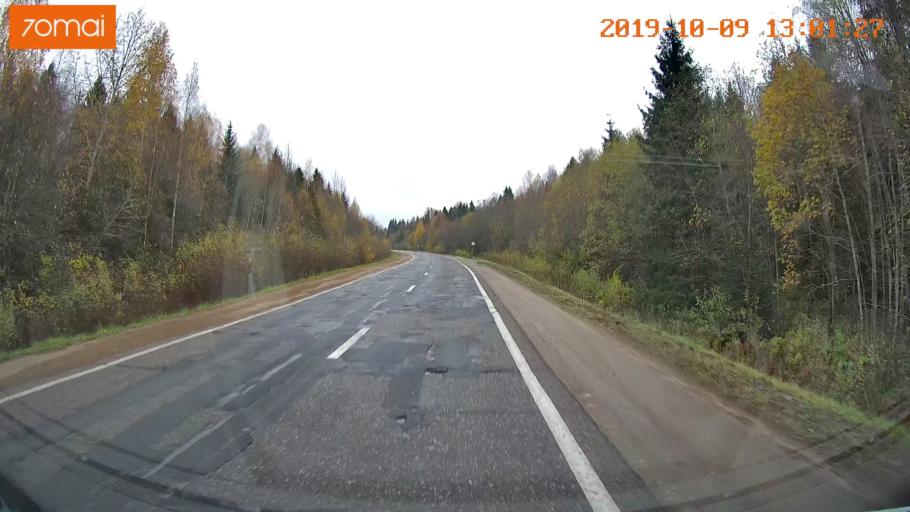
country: RU
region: Jaroslavl
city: Prechistoye
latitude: 58.3682
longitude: 40.4866
